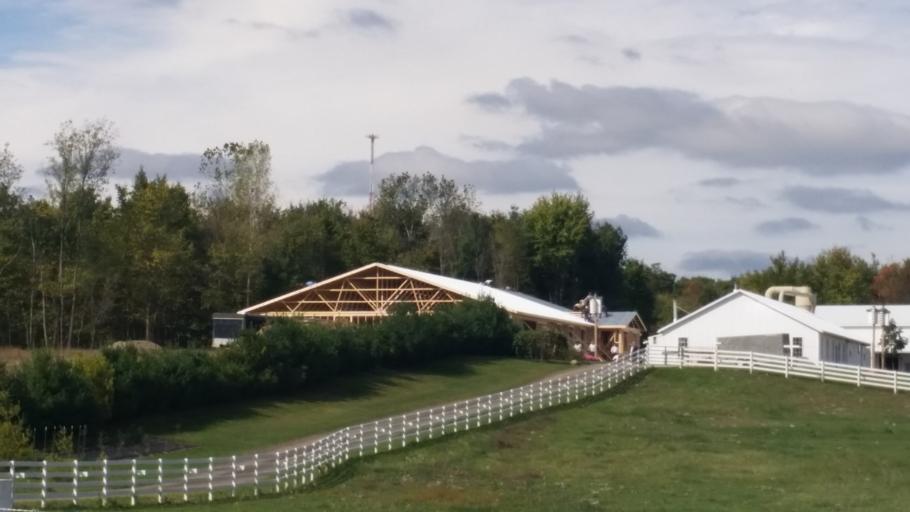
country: US
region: Ohio
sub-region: Knox County
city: Fredericktown
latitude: 40.5211
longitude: -82.6513
